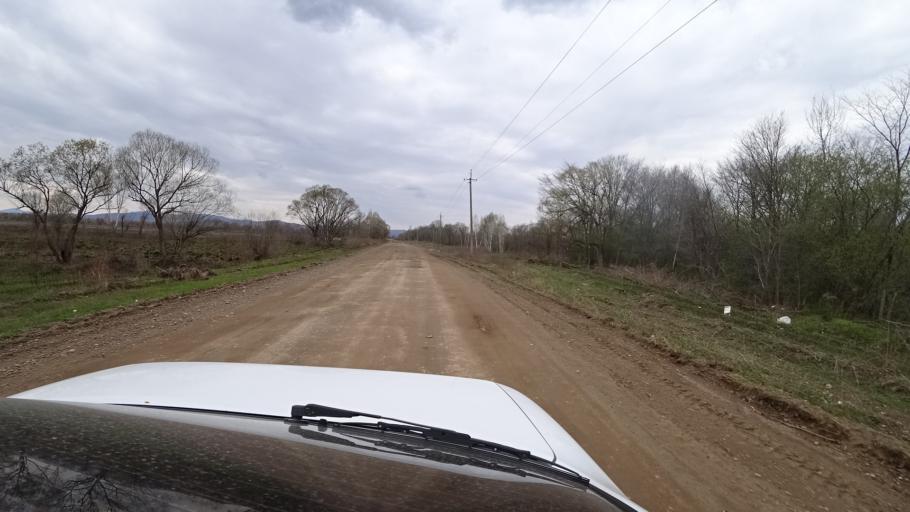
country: RU
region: Primorskiy
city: Novopokrovka
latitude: 45.5586
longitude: 134.3504
